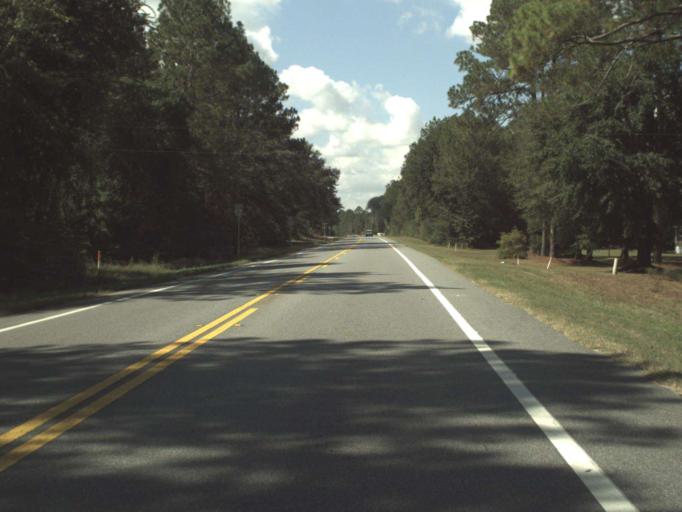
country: US
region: Florida
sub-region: Walton County
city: Freeport
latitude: 30.4722
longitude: -85.9656
